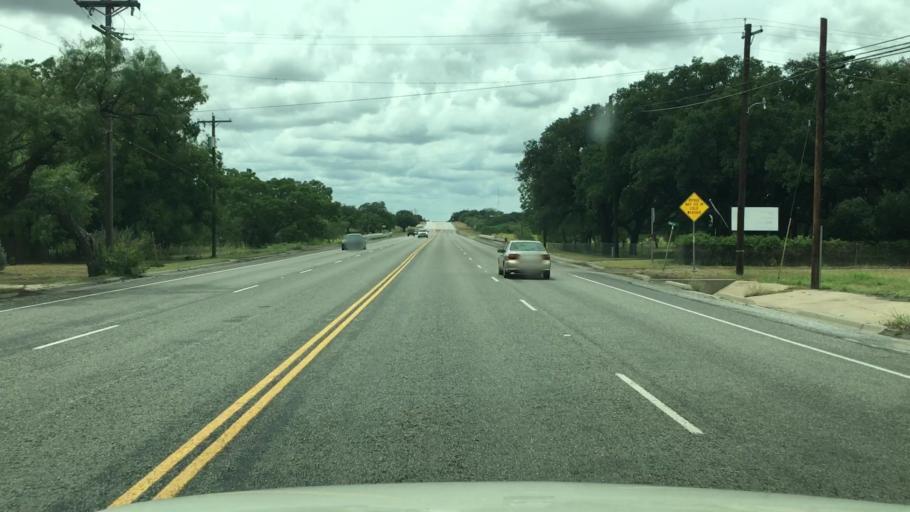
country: US
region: Texas
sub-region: Concho County
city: Eden
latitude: 31.2164
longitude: -99.8513
